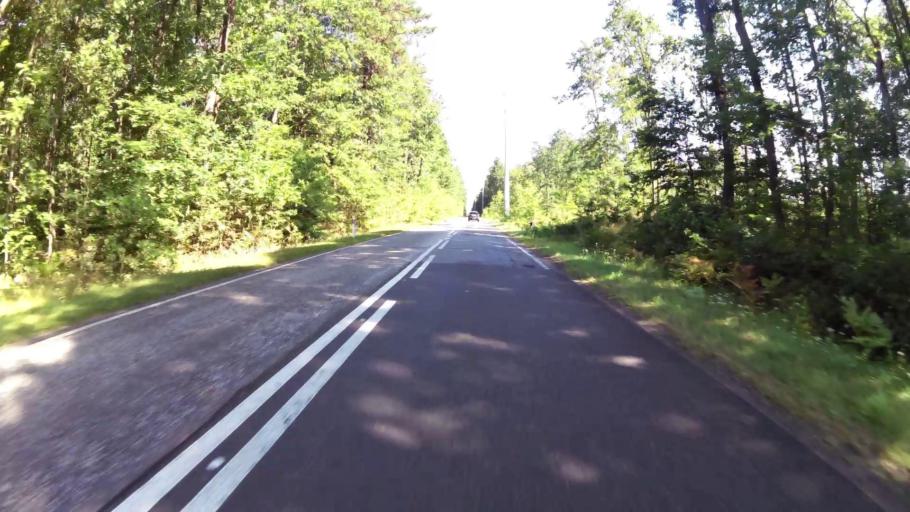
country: PL
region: West Pomeranian Voivodeship
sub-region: Powiat drawski
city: Czaplinek
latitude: 53.4477
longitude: 16.2124
